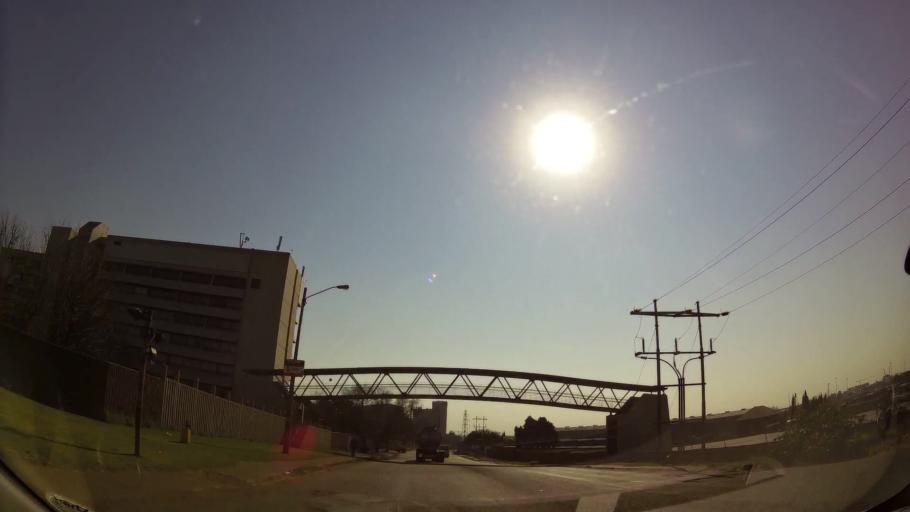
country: ZA
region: Gauteng
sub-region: City of Johannesburg Metropolitan Municipality
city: Modderfontein
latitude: -26.1396
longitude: 28.2146
